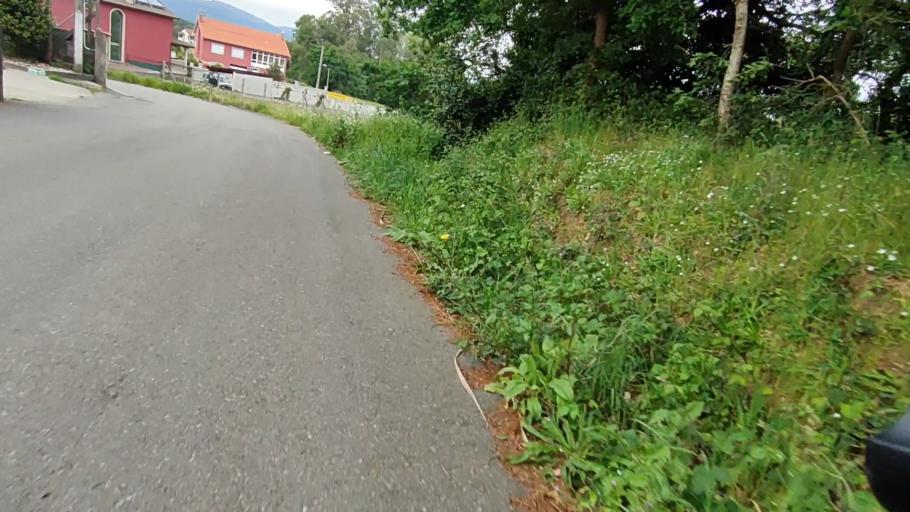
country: ES
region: Galicia
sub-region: Provincia da Coruna
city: Boiro
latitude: 42.6315
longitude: -8.8631
